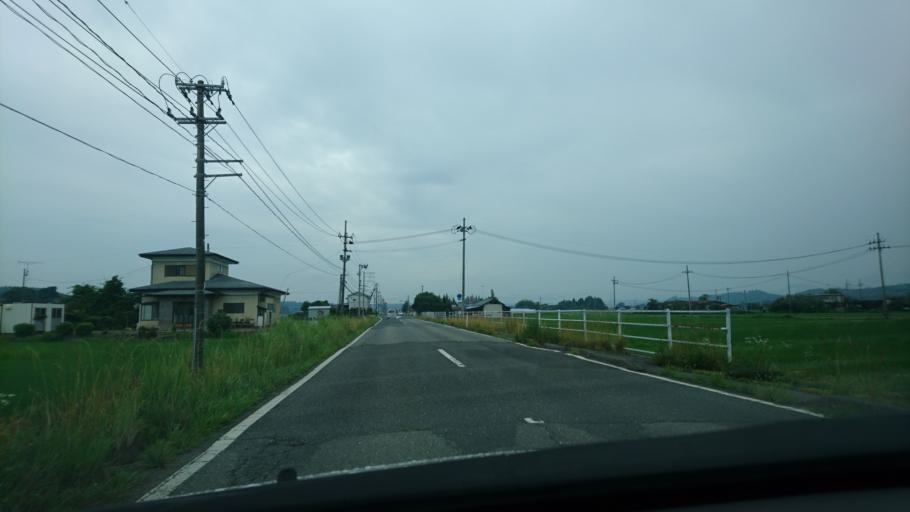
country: JP
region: Miyagi
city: Furukawa
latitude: 38.7315
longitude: 140.9740
